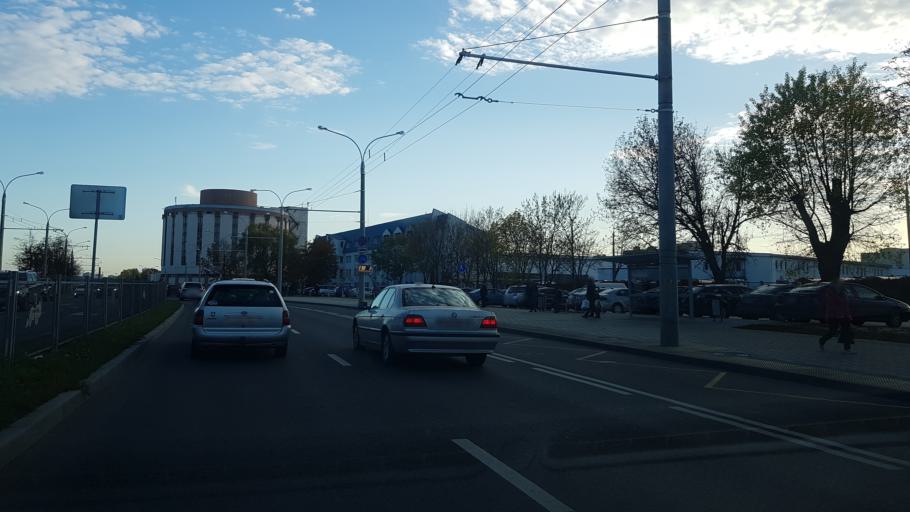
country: BY
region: Minsk
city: Minsk
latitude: 53.9027
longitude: 27.5337
